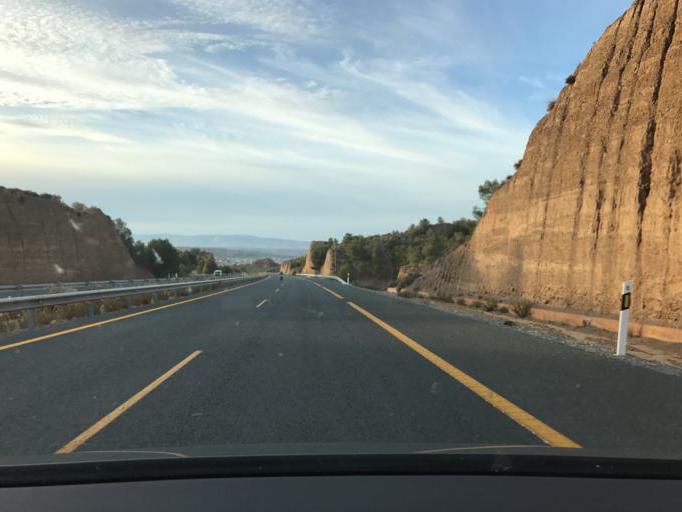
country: ES
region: Andalusia
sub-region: Provincia de Granada
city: Guadix
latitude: 37.2848
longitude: -3.1021
